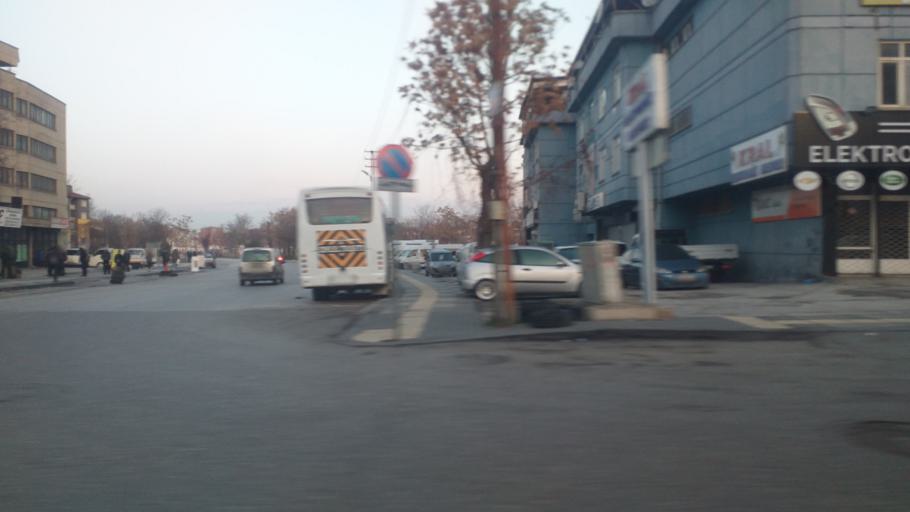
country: TR
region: Ankara
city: Ankara
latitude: 39.9513
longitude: 32.8540
